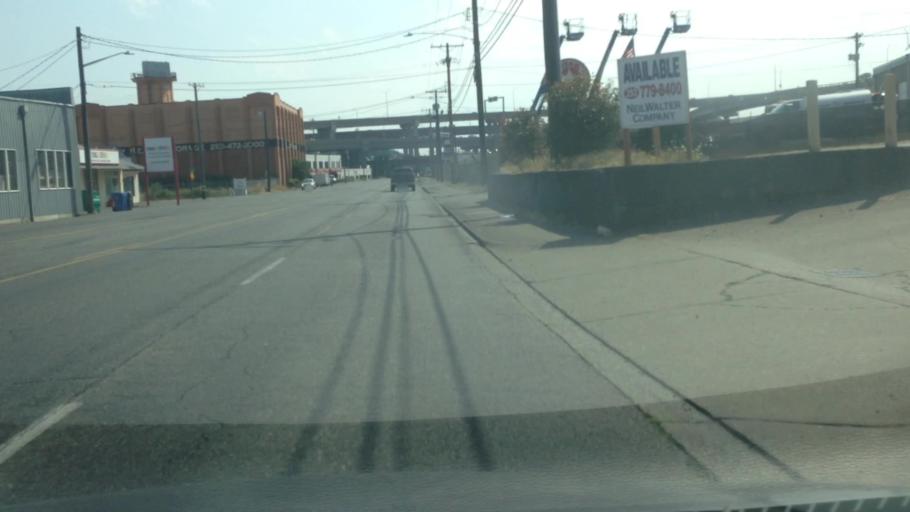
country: US
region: Washington
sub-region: Pierce County
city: Tacoma
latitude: 47.2313
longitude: -122.4683
